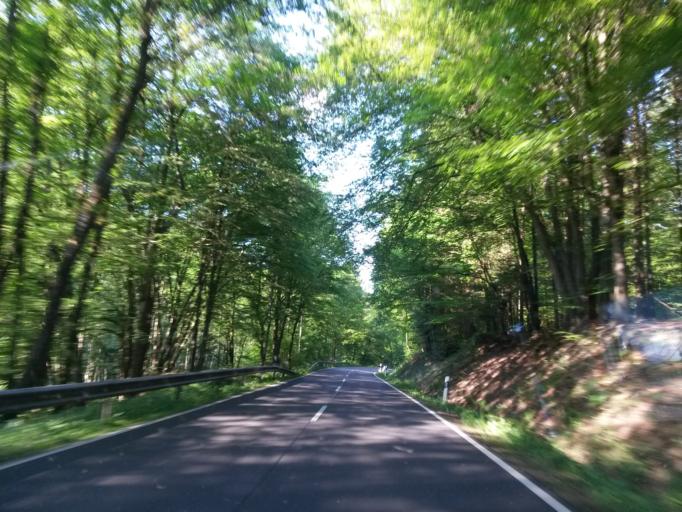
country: DE
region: North Rhine-Westphalia
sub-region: Regierungsbezirk Koln
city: Much
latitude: 50.8683
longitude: 7.3433
